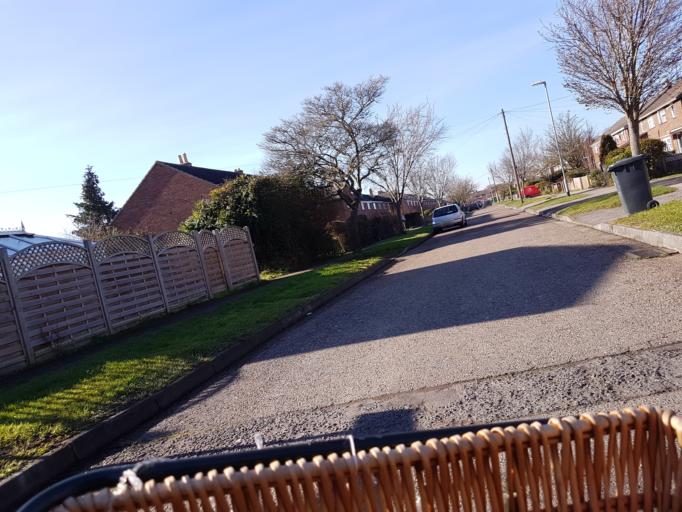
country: GB
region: England
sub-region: Cambridgeshire
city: Fulbourn
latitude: 52.1846
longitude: 0.1809
